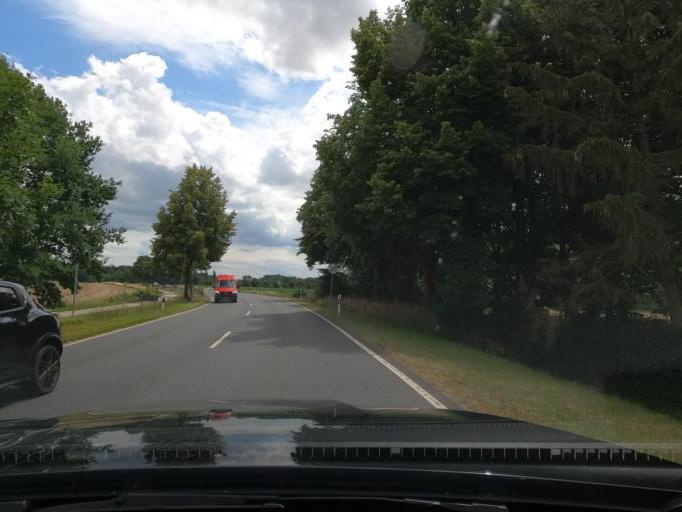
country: DE
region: Lower Saxony
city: Sehnde
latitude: 52.3378
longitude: 9.9323
